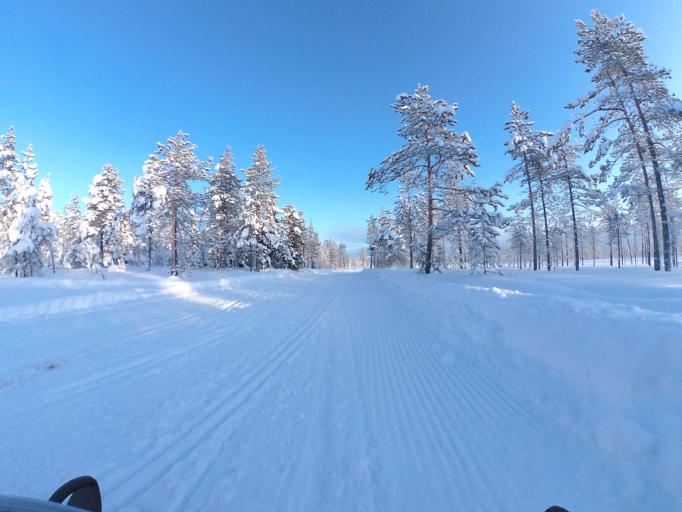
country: FI
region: Lapland
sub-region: Rovaniemi
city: Rovaniemi
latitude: 66.5432
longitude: 25.8688
